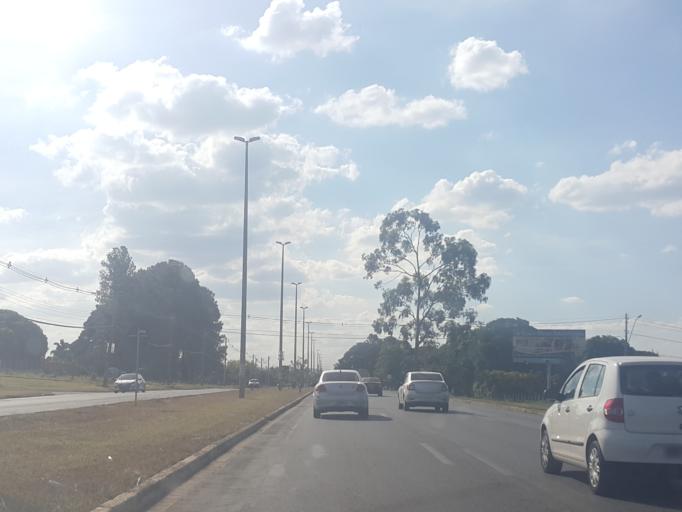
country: BR
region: Federal District
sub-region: Brasilia
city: Brasilia
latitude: -15.8327
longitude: -48.0059
